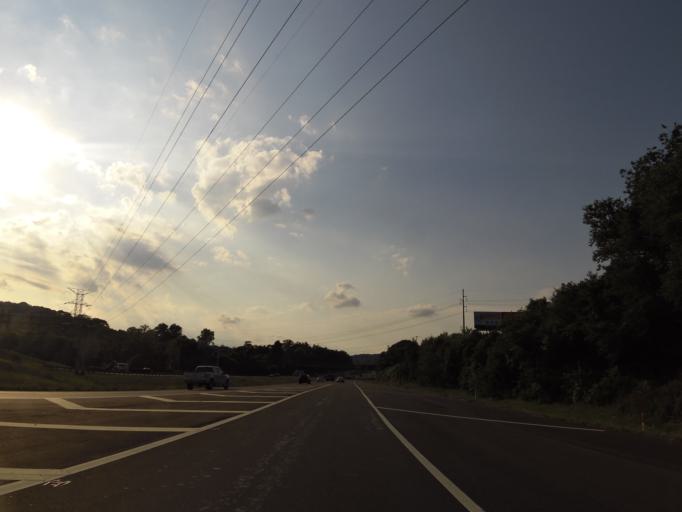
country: US
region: Tennessee
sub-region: Knox County
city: Knoxville
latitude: 35.9592
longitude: -83.9719
